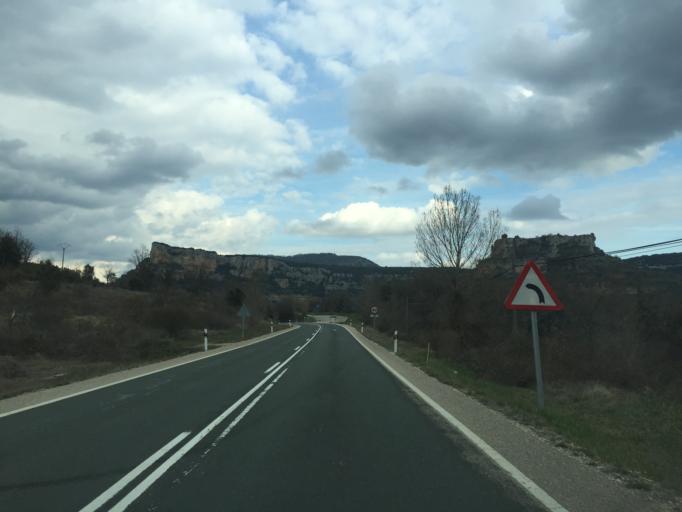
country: ES
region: Castille and Leon
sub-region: Provincia de Burgos
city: Tubilla del Agua
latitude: 42.7740
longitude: -3.7755
